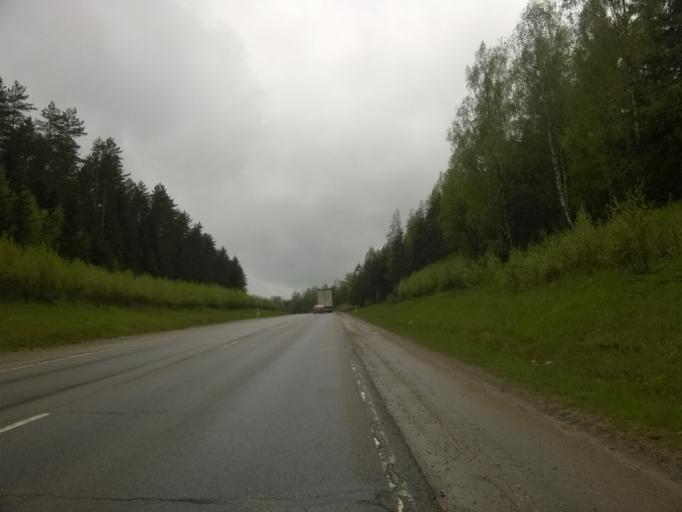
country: LV
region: Amatas Novads
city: Drabesi
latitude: 57.2210
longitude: 25.2217
